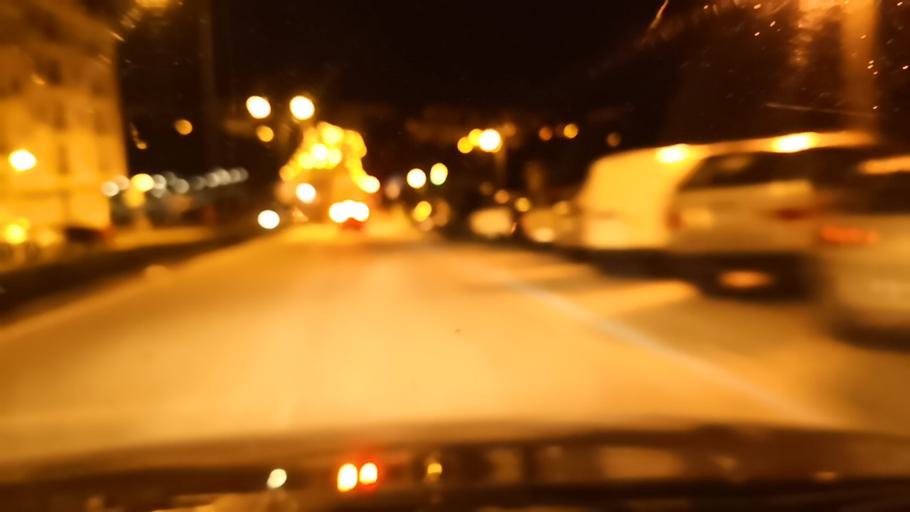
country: PT
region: Castelo Branco
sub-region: Concelho do Fundao
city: Fundao
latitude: 40.1445
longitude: -7.5017
